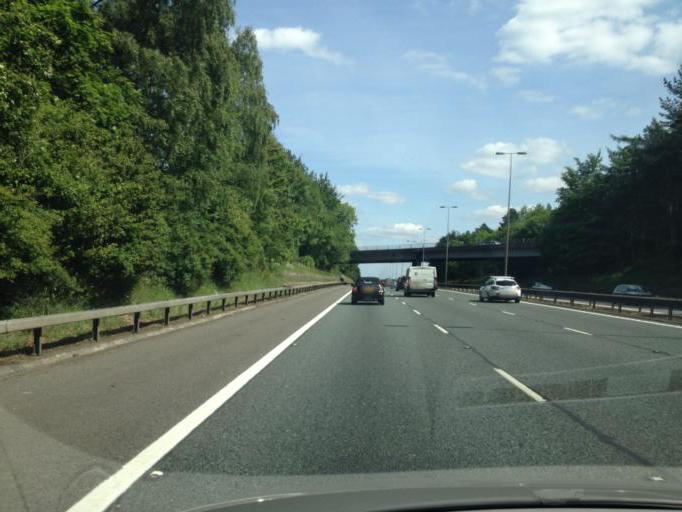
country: GB
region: England
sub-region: Buckinghamshire
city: Marlow
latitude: 51.6227
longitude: -0.8206
